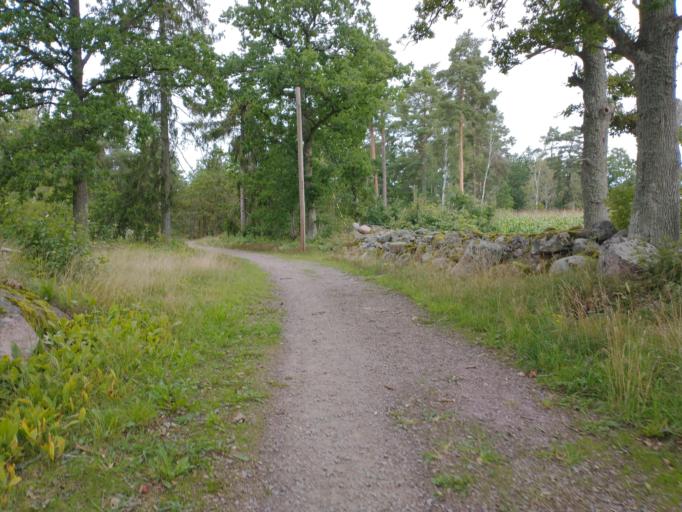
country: SE
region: Kalmar
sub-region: Kalmar Kommun
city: Lindsdal
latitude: 56.7765
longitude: 16.2999
